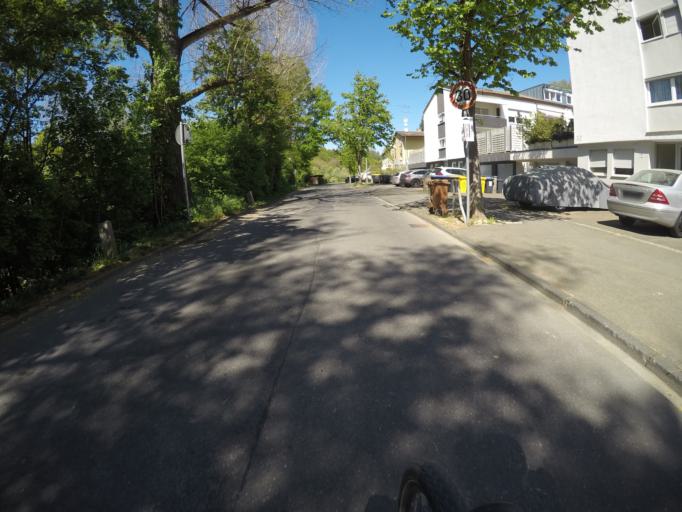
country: DE
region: Baden-Wuerttemberg
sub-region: Regierungsbezirk Stuttgart
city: Waiblingen
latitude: 48.8398
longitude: 9.3129
